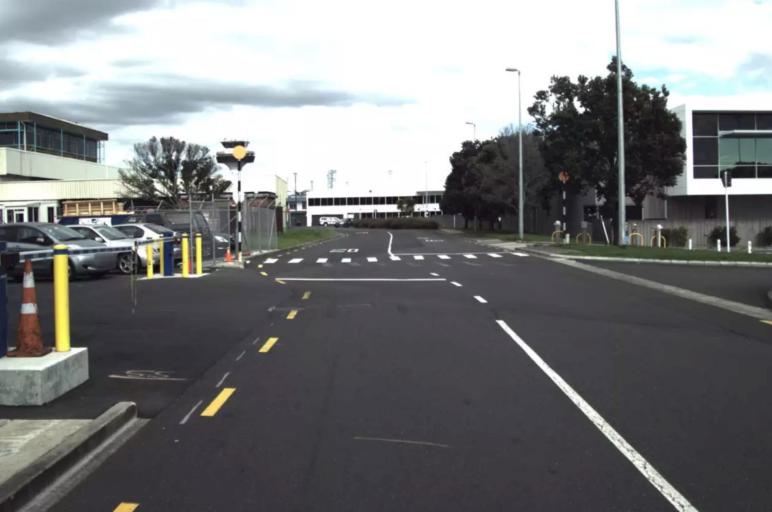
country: NZ
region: Auckland
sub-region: Auckland
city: Mangere
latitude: -37.0040
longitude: 174.7873
